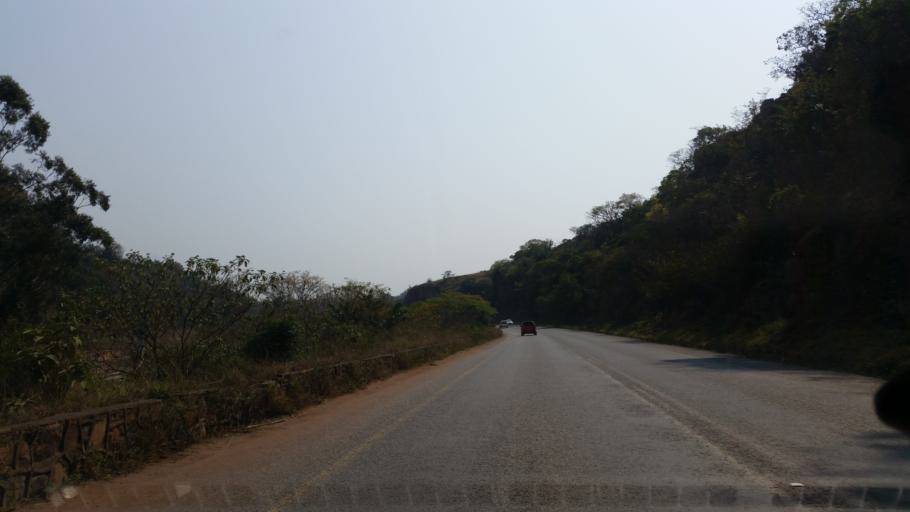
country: ZA
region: KwaZulu-Natal
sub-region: eThekwini Metropolitan Municipality
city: Mpumalanga
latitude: -29.7529
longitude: 30.6657
